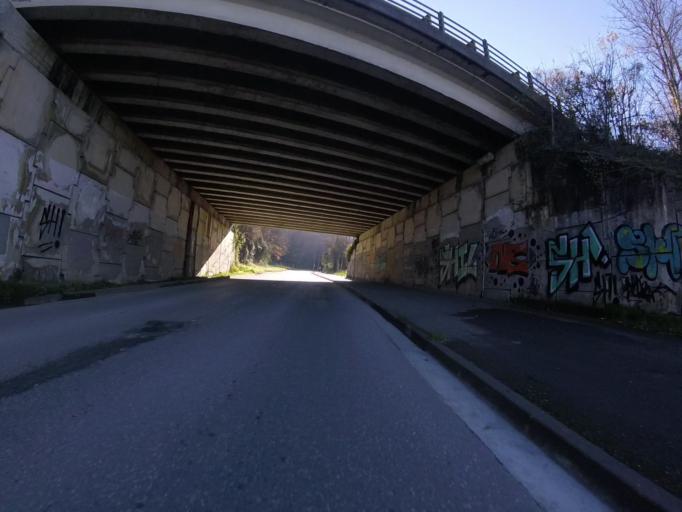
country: ES
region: Basque Country
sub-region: Provincia de Guipuzcoa
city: Irun
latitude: 43.3342
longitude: -1.7775
